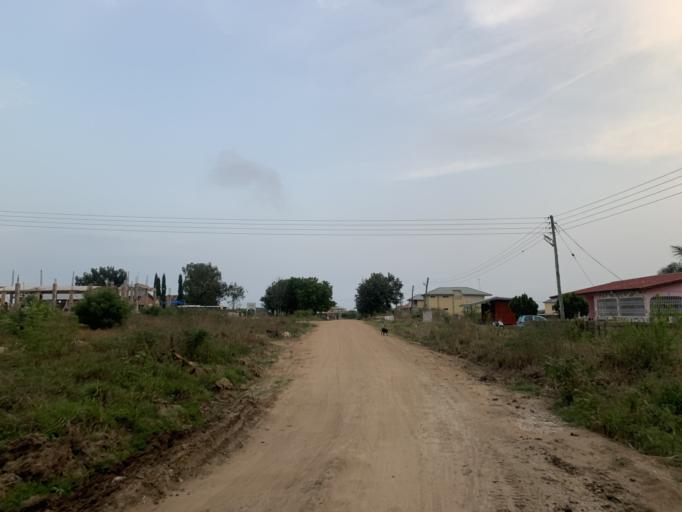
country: GH
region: Central
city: Winneba
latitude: 5.3790
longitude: -0.6334
